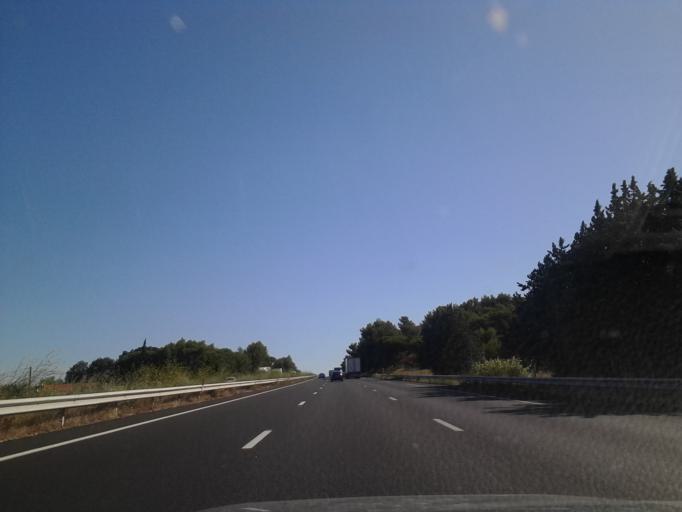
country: FR
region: Languedoc-Roussillon
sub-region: Departement de l'Aude
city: Vinassan
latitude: 43.1991
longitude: 3.0781
